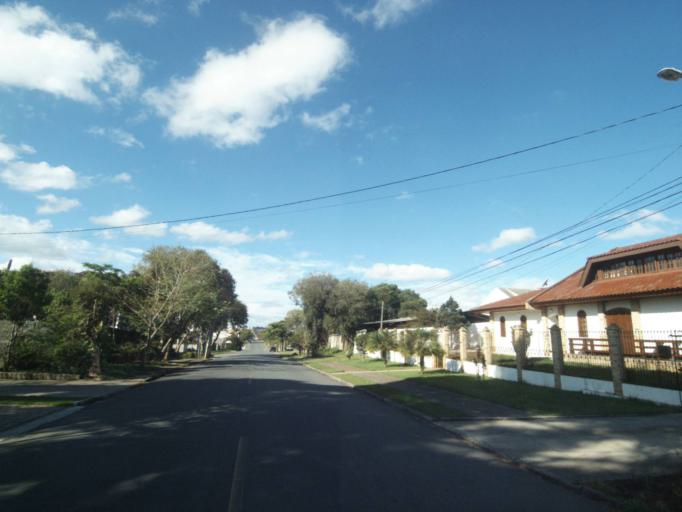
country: BR
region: Parana
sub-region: Curitiba
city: Curitiba
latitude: -25.3906
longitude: -49.2533
